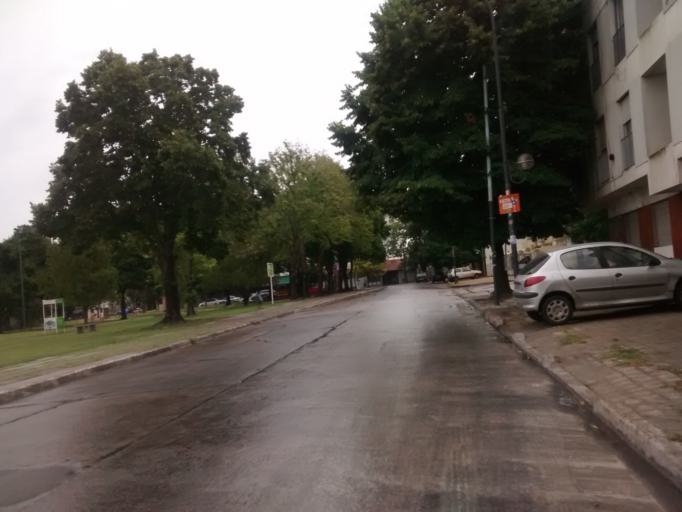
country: AR
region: Buenos Aires
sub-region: Partido de La Plata
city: La Plata
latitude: -34.9370
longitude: -57.9462
